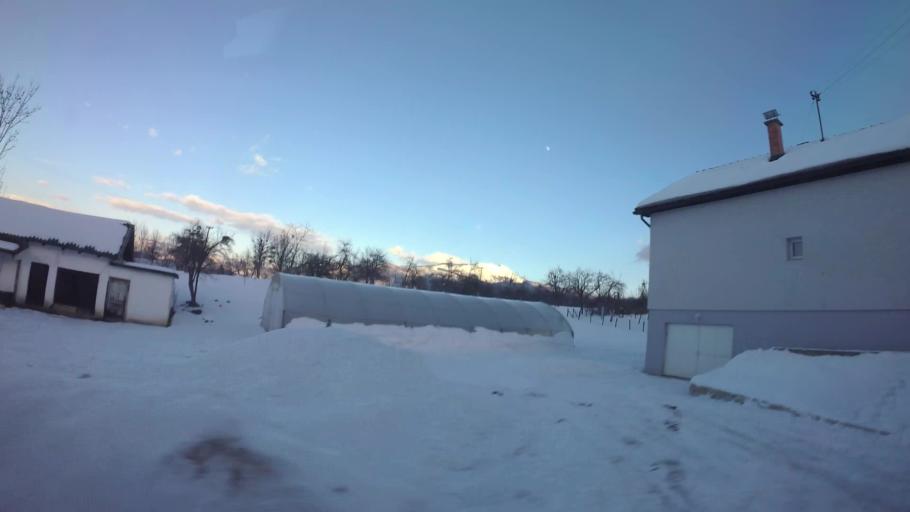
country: BA
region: Federation of Bosnia and Herzegovina
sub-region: Kanton Sarajevo
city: Sarajevo
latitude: 43.8100
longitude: 18.3543
